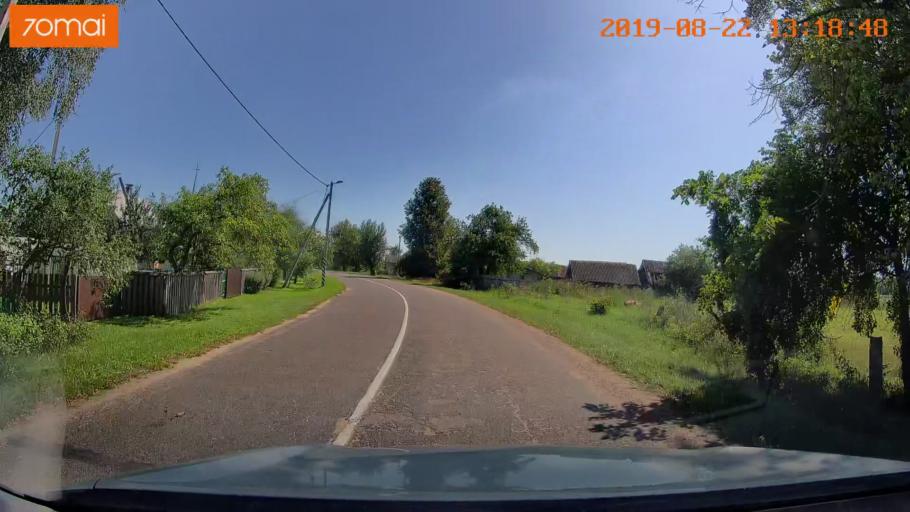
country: BY
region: Minsk
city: Urechcha
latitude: 53.2382
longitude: 27.9429
